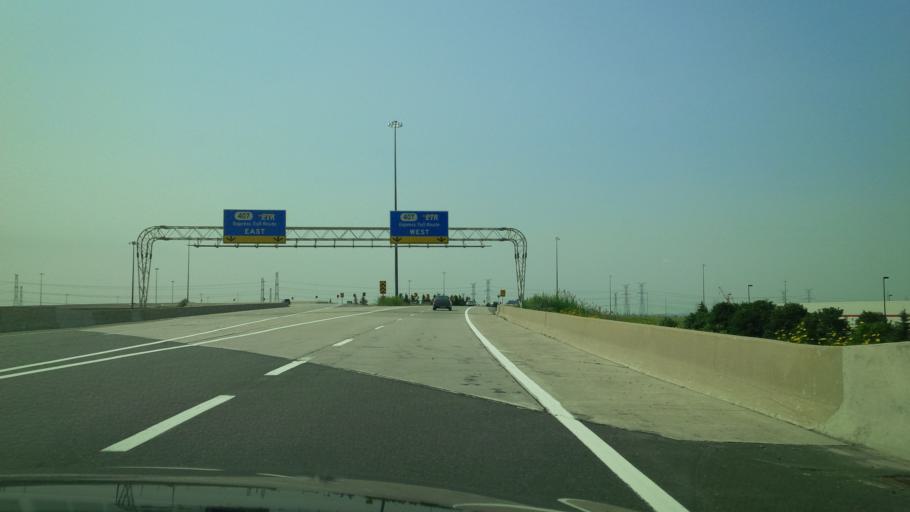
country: CA
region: Ontario
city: Concord
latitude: 43.7869
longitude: -79.5396
